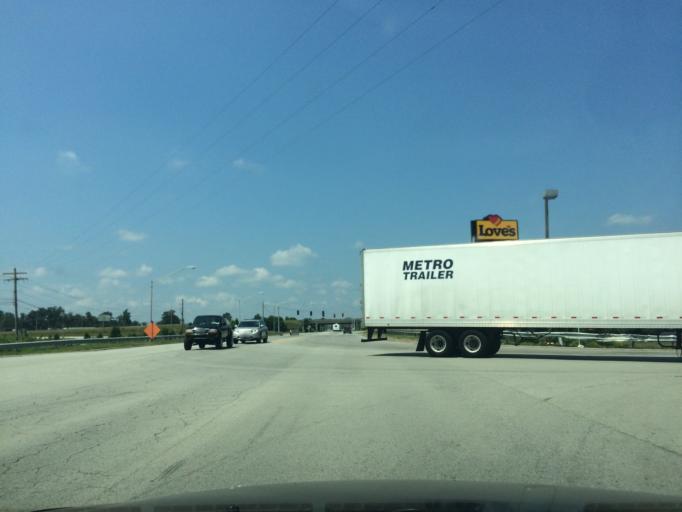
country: US
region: Kentucky
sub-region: Bullitt County
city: Shepherdsville
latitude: 37.9787
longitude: -85.6929
